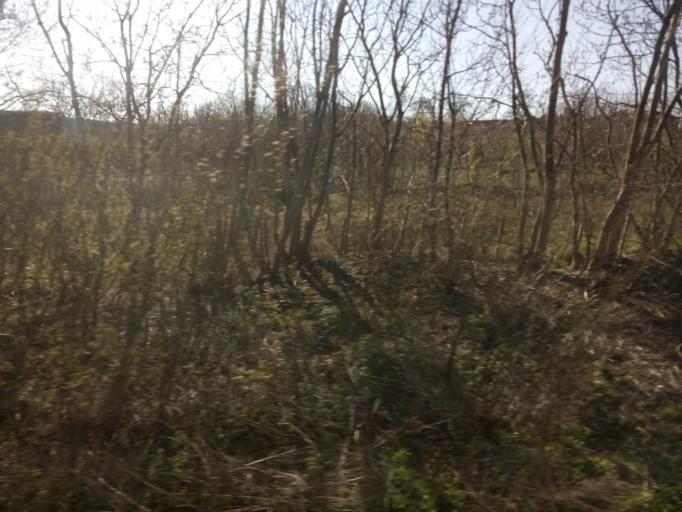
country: GB
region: Scotland
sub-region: The Scottish Borders
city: Eyemouth
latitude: 55.8392
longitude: -2.1113
